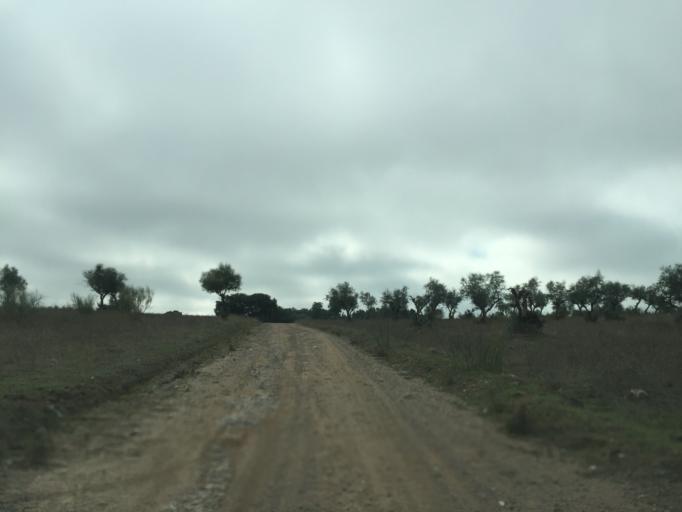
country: PT
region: Portalegre
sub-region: Fronteira
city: Fronteira
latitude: 39.0573
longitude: -7.6328
